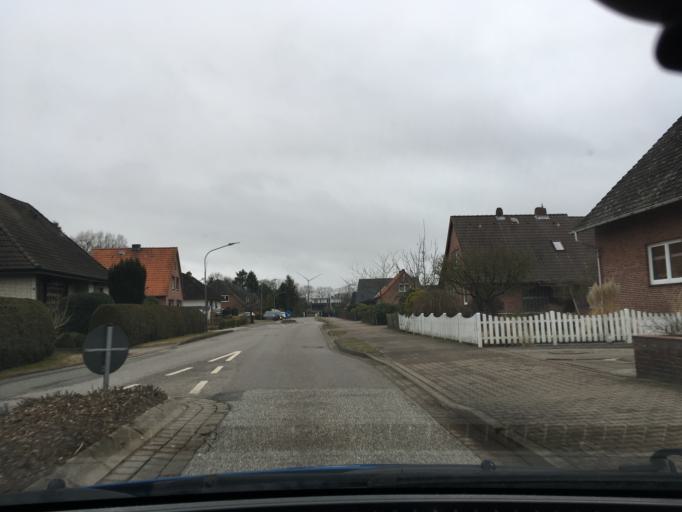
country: DE
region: Lower Saxony
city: Winsen
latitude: 53.3415
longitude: 10.2084
